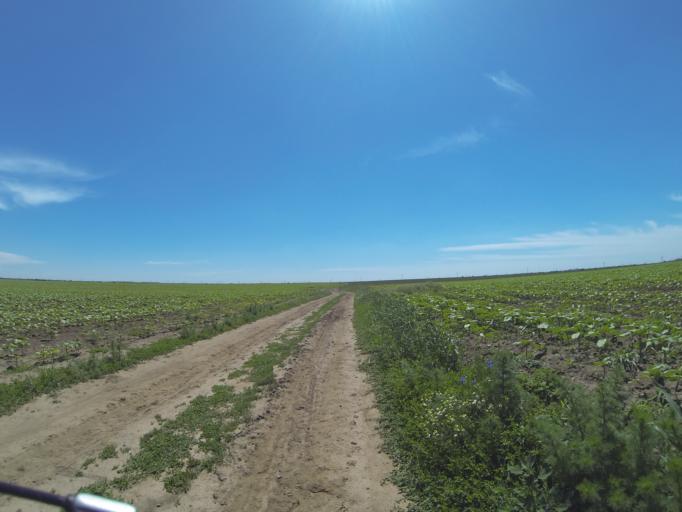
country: RO
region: Dolj
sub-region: Comuna Leu
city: Zanoaga
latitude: 44.1981
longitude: 24.0623
